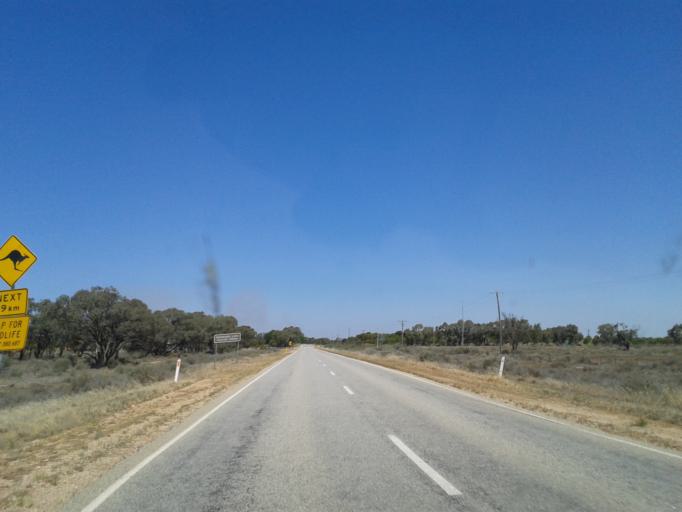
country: AU
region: Victoria
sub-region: Swan Hill
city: Swan Hill
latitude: -34.7777
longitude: 143.2455
